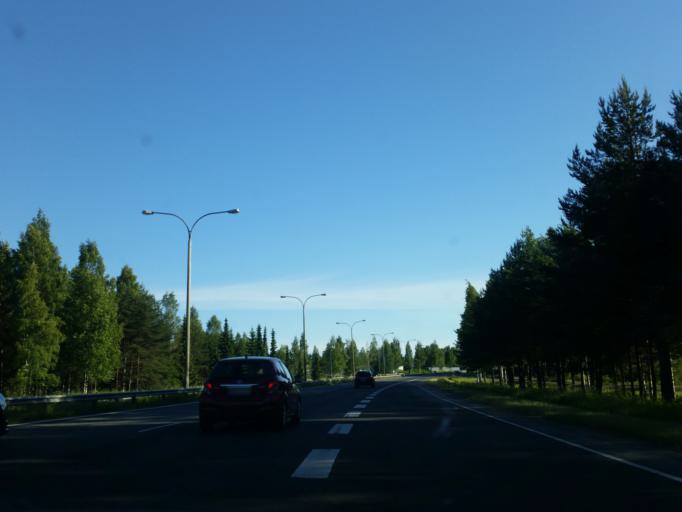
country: FI
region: Northern Savo
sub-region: Kuopio
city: Kuopio
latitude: 62.8833
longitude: 27.6348
